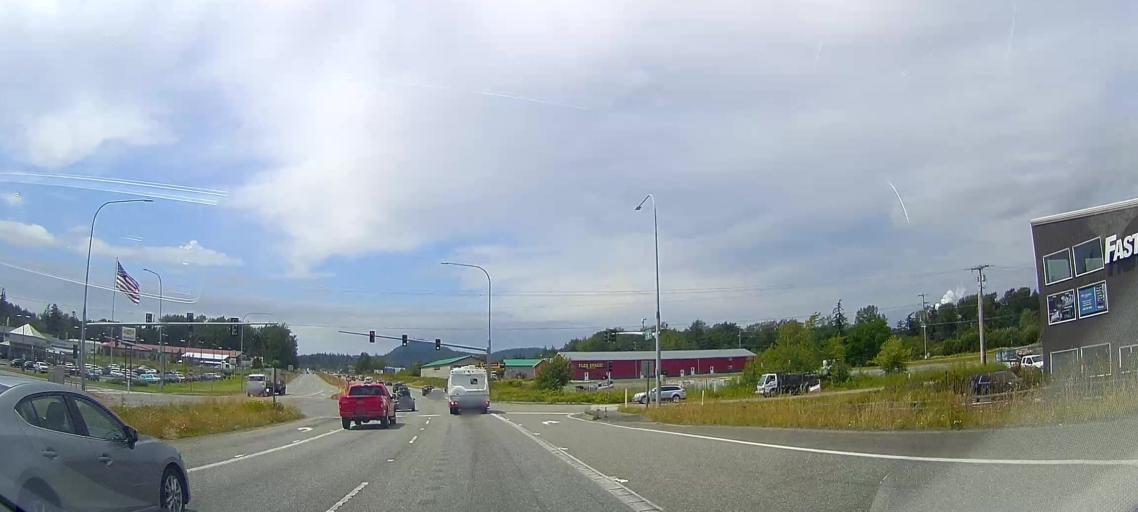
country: US
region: Washington
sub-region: Skagit County
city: Anacortes
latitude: 48.4633
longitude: -122.5433
